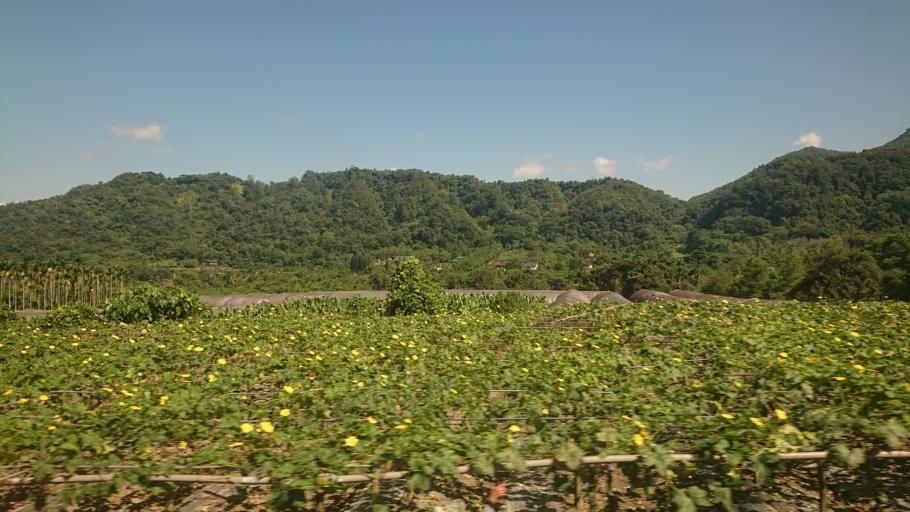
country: TW
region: Taiwan
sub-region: Nantou
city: Puli
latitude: 24.0610
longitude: 120.9421
